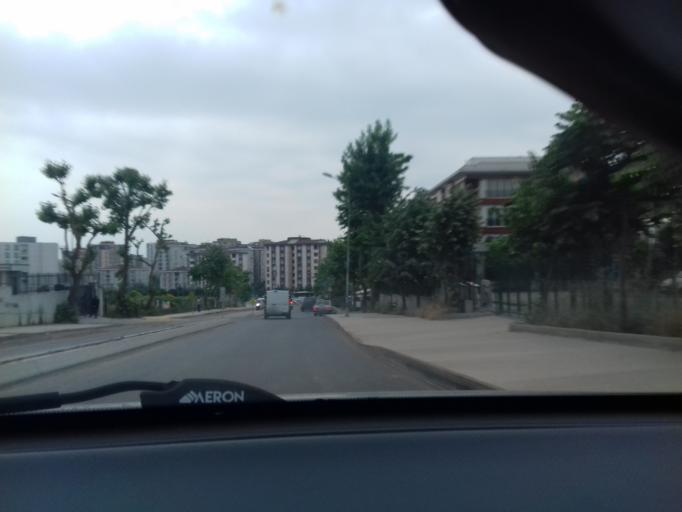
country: TR
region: Istanbul
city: Sultanbeyli
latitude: 40.9319
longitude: 29.2955
